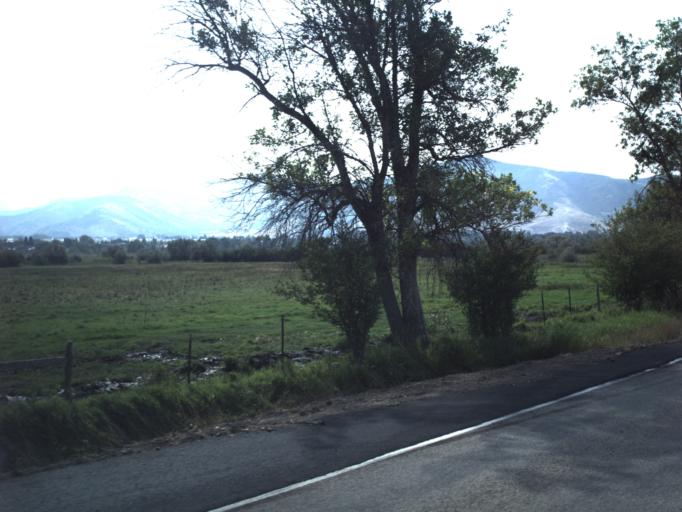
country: US
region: Utah
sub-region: Wasatch County
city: Midway
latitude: 40.4928
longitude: -111.4720
